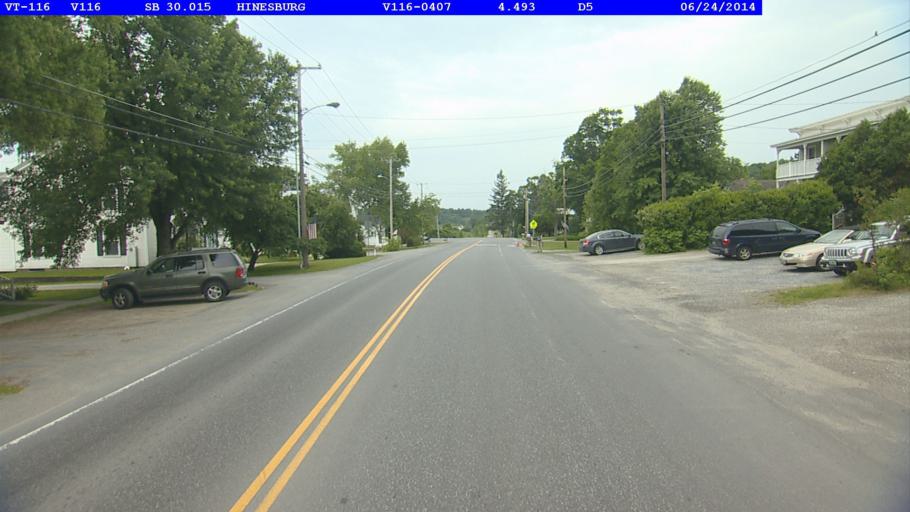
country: US
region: Vermont
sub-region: Chittenden County
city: Hinesburg
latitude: 44.3281
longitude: -73.1101
